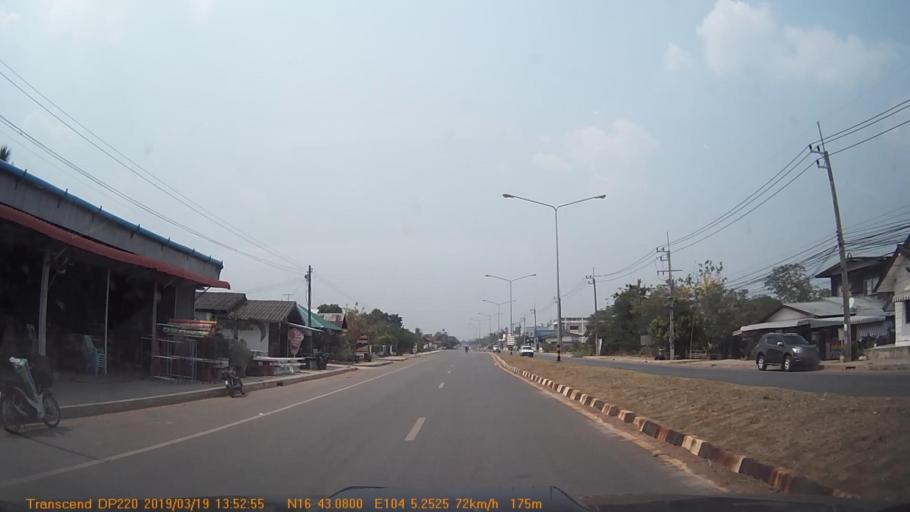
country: TH
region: Kalasin
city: Khao Wong
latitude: 16.7184
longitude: 104.0874
